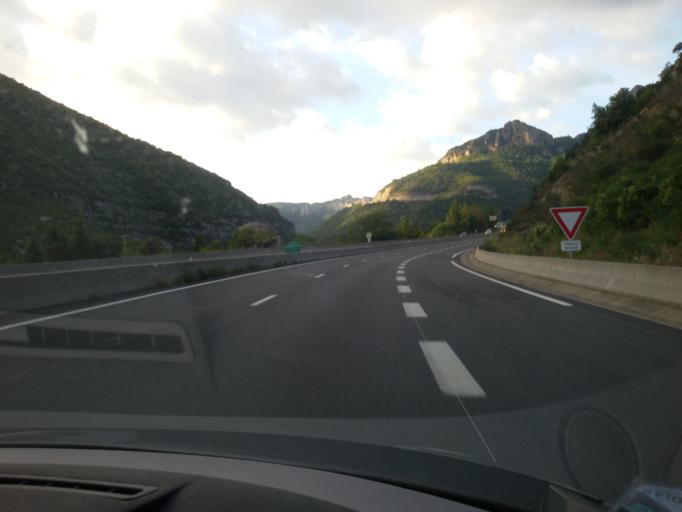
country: FR
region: Languedoc-Roussillon
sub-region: Departement de l'Herault
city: Lodeve
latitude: 43.7980
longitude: 3.3257
